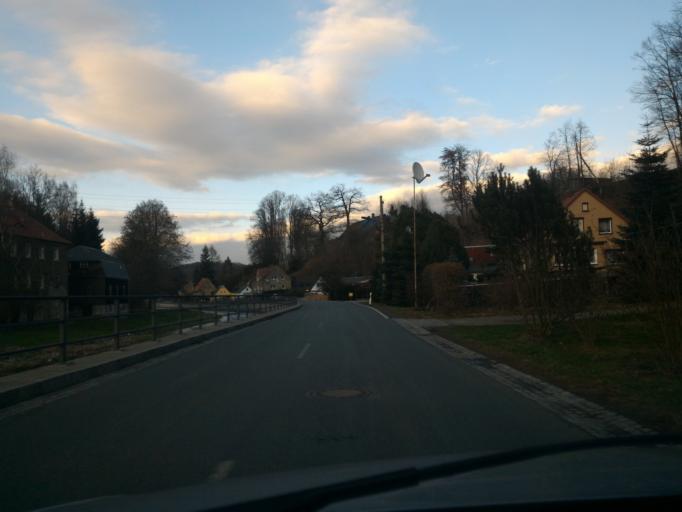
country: DE
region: Saxony
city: Hainewalde
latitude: 50.9117
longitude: 14.7073
